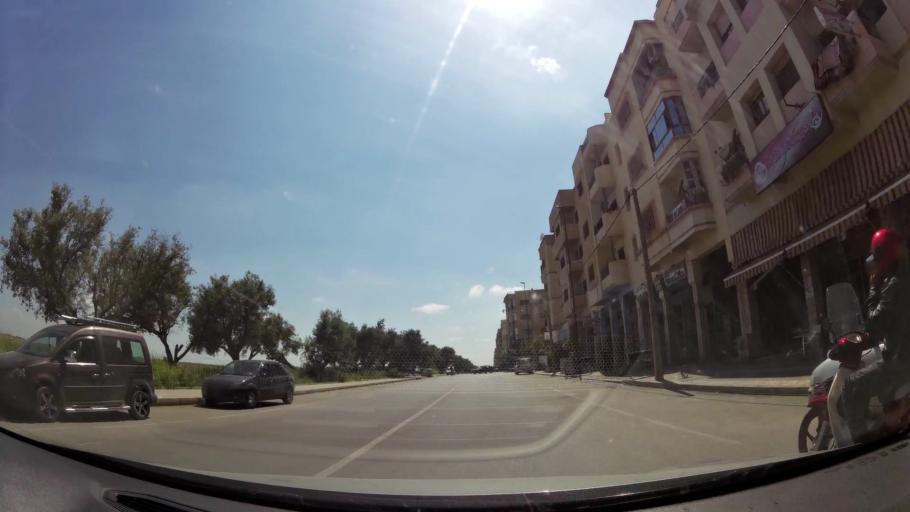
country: MA
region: Fes-Boulemane
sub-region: Fes
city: Fes
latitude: 34.0098
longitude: -5.0252
